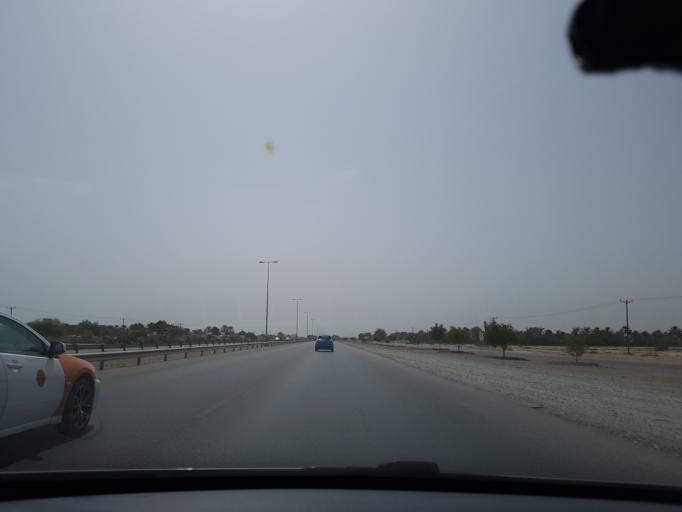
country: OM
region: Al Batinah
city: As Suwayq
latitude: 23.8158
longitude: 57.4510
